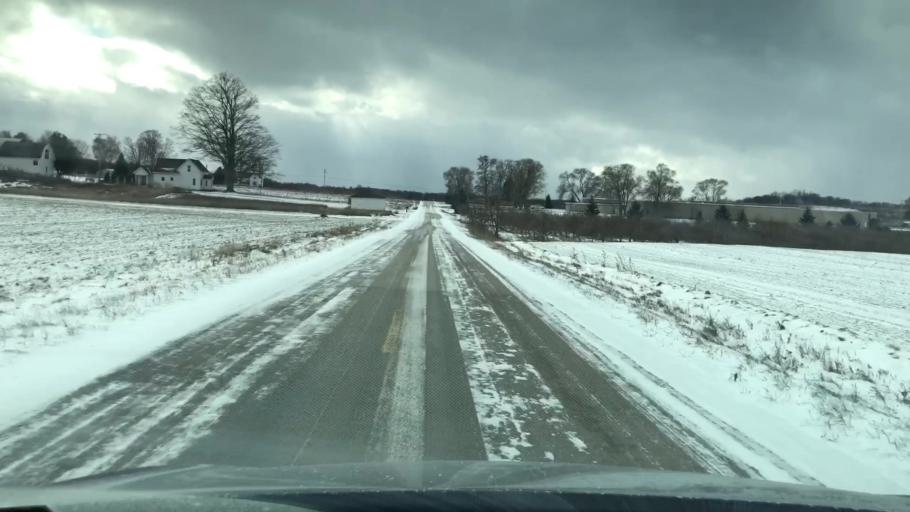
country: US
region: Michigan
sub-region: Antrim County
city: Elk Rapids
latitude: 44.9246
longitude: -85.5156
